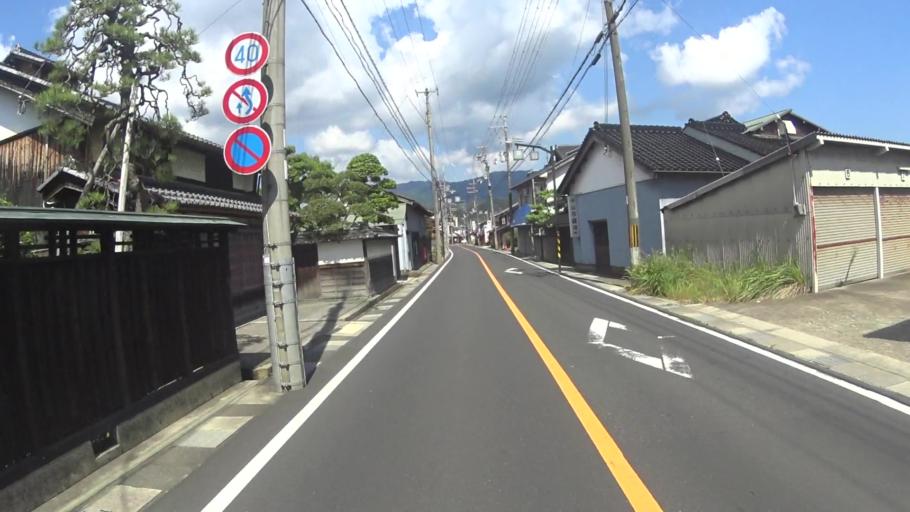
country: JP
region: Kyoto
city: Miyazu
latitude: 35.5665
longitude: 135.1532
